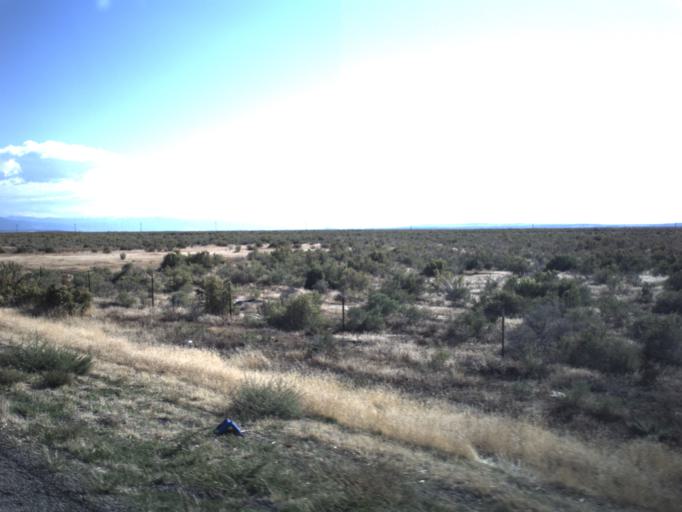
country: US
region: Utah
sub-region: Millard County
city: Delta
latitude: 39.2461
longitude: -112.4366
